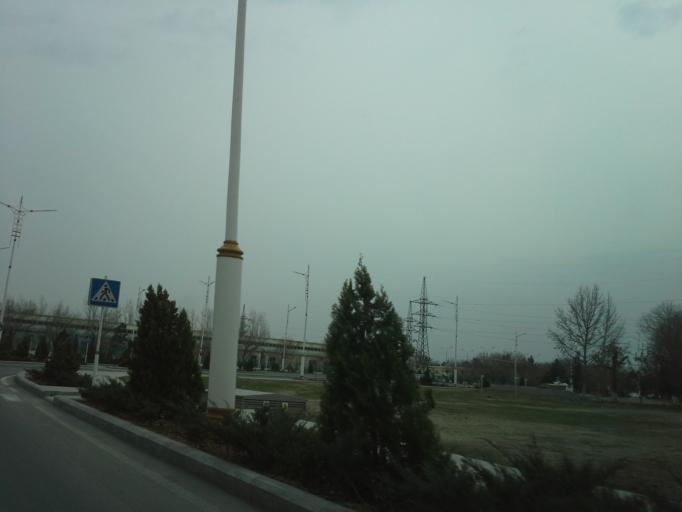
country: TM
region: Ahal
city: Ashgabat
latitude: 37.9628
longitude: 58.3616
